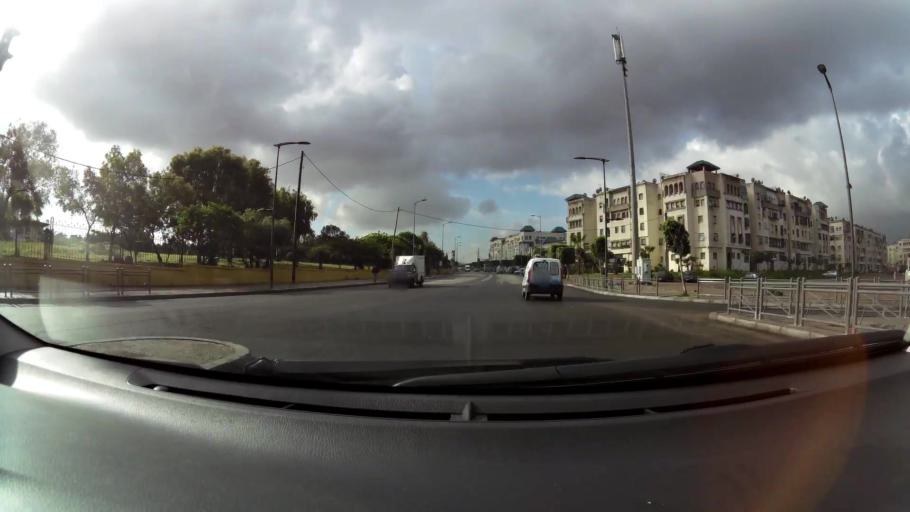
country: MA
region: Grand Casablanca
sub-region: Mediouna
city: Tit Mellil
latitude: 33.5997
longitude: -7.5310
